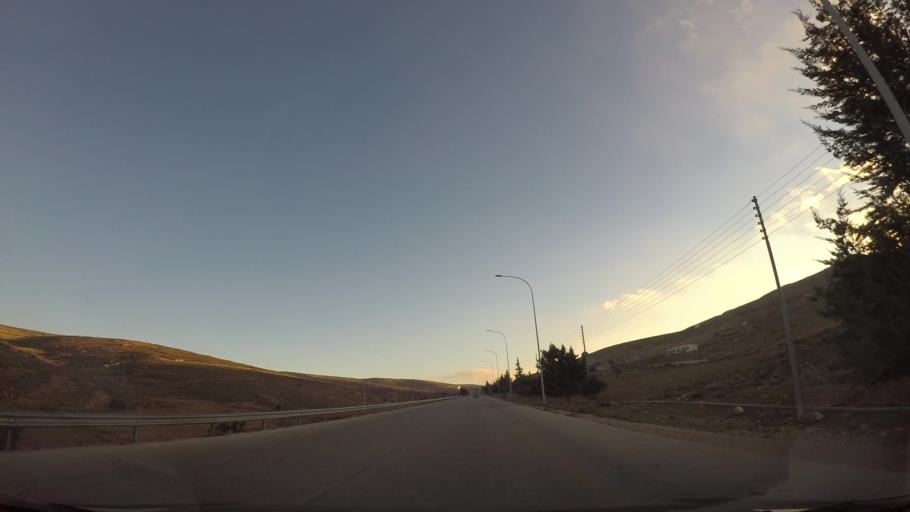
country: JO
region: Ma'an
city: Petra
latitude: 30.4296
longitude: 35.5151
